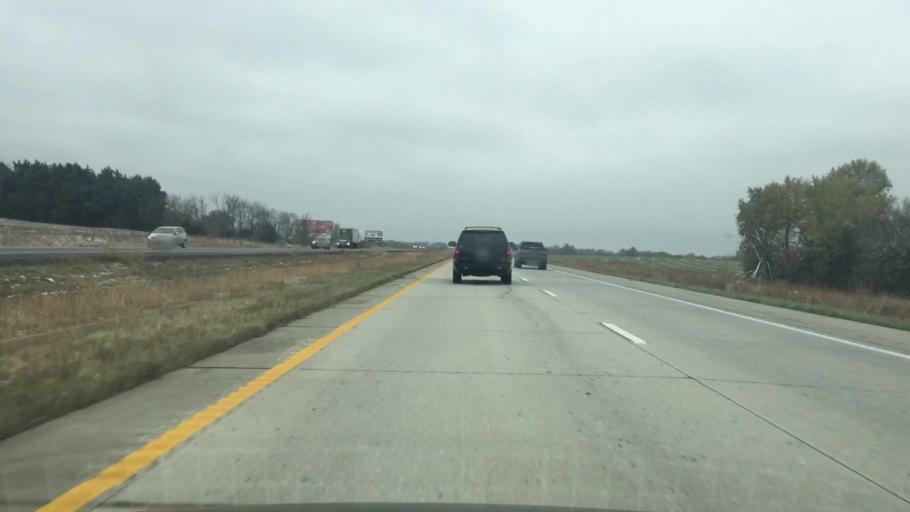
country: US
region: Missouri
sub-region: Saint Clair County
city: Osceola
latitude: 37.9988
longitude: -93.6550
